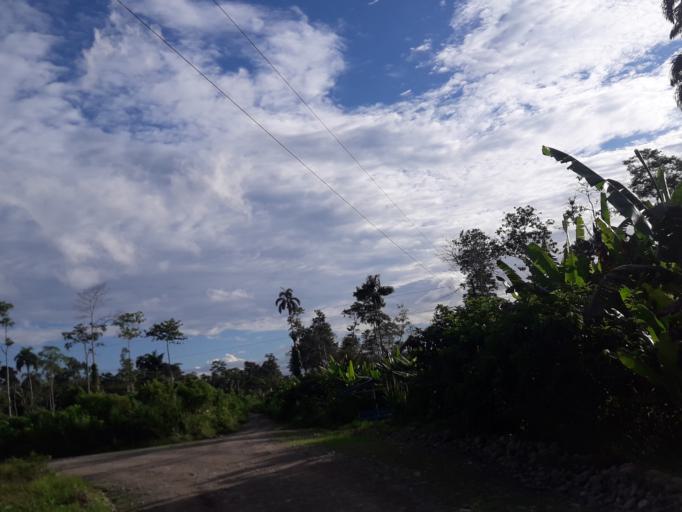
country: EC
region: Orellana
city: Boca Suno
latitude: -0.8858
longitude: -77.2990
